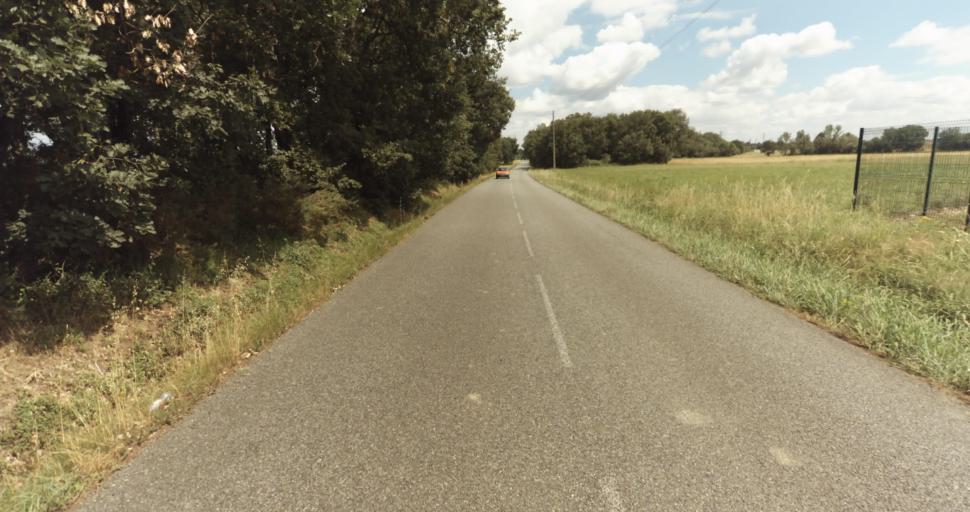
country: FR
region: Midi-Pyrenees
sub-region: Departement de la Haute-Garonne
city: Fontenilles
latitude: 43.5618
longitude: 1.1945
